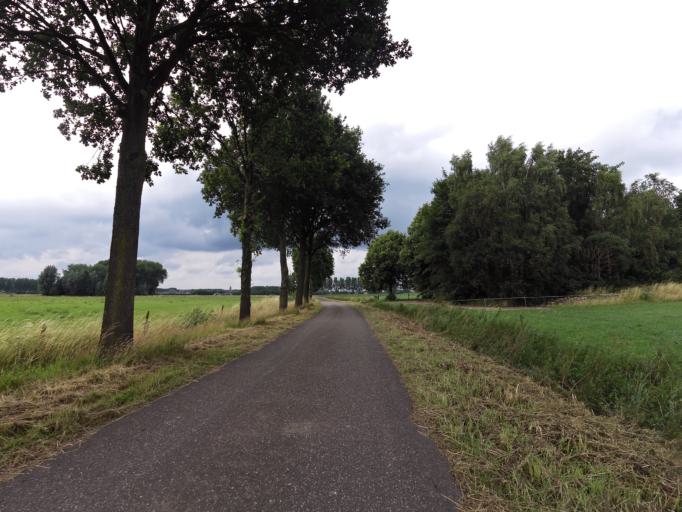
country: NL
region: Gelderland
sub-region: Gemeente Rheden
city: De Steeg
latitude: 51.9845
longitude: 6.0747
